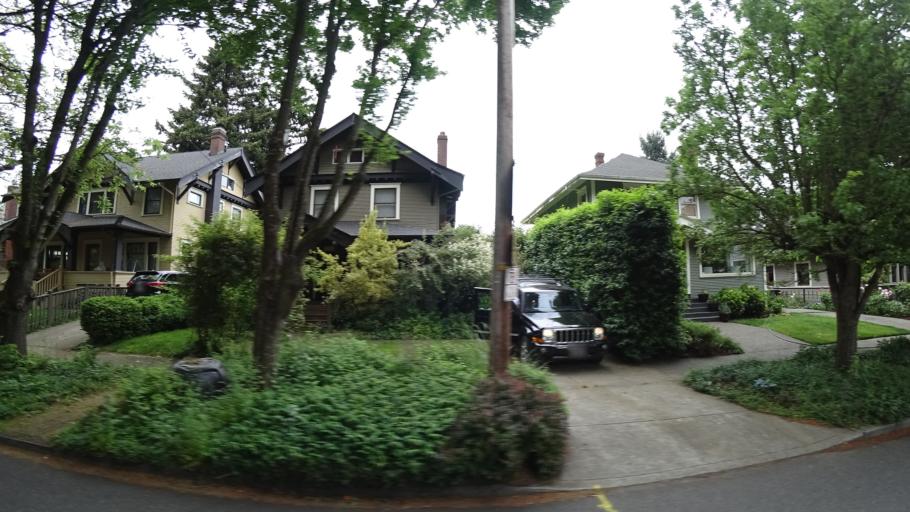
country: US
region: Oregon
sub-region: Multnomah County
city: Portland
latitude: 45.5400
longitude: -122.6150
